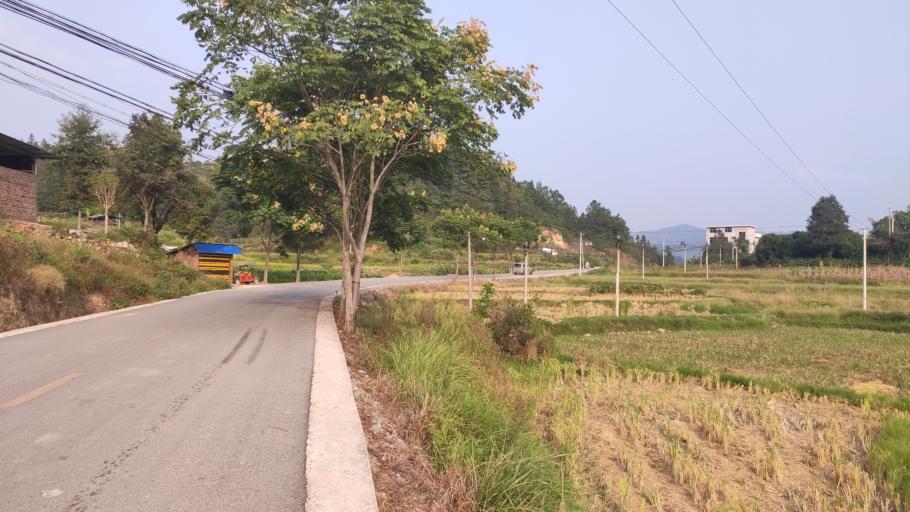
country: CN
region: Guizhou Sheng
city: Zhongchao
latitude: 26.1512
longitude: 109.2066
